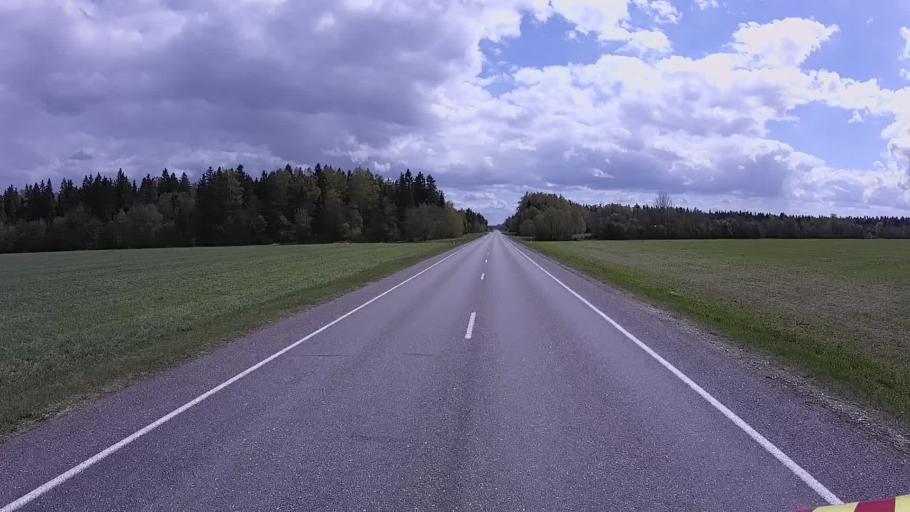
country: EE
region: Jaervamaa
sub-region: Jaerva-Jaani vald
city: Jarva-Jaani
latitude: 59.1363
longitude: 25.7733
